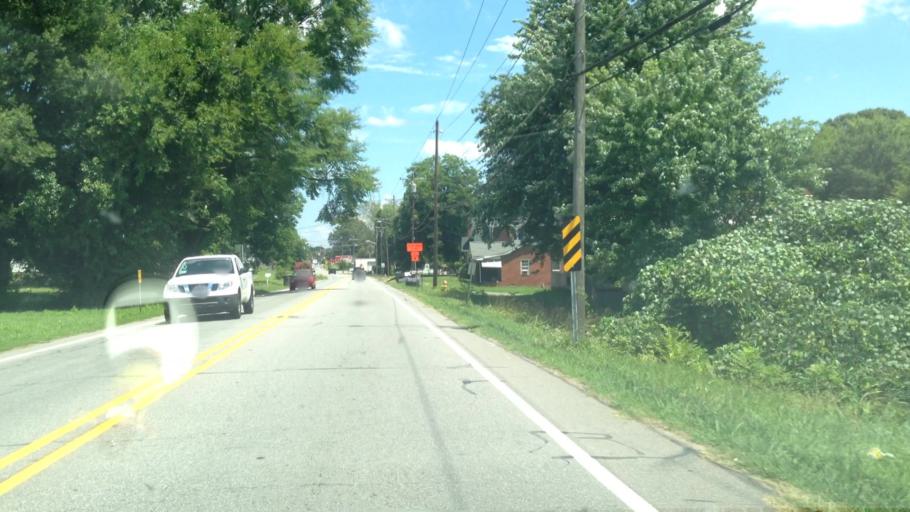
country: US
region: North Carolina
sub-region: Rockingham County
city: Reidsville
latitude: 36.3549
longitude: -79.6734
